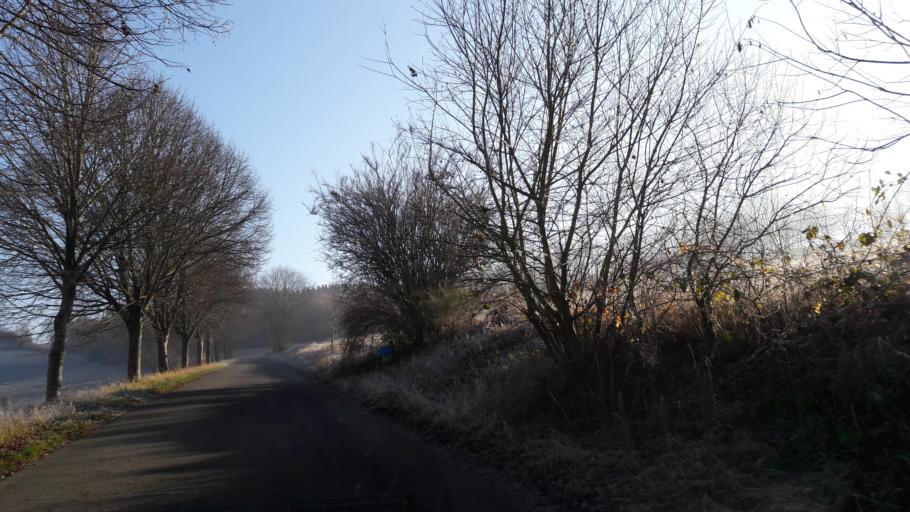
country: DE
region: Rheinland-Pfalz
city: Breitenbach
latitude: 49.4728
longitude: 7.2614
